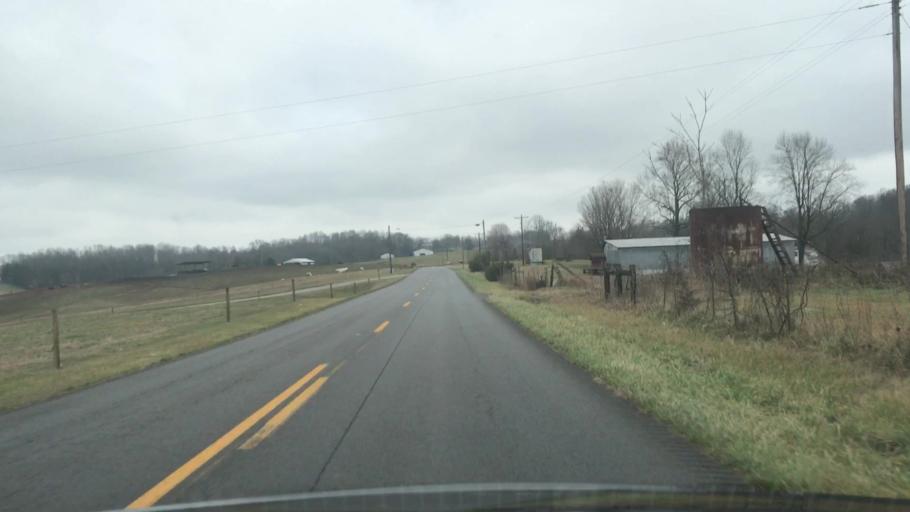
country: US
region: Kentucky
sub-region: Monroe County
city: Tompkinsville
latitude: 36.7928
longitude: -85.7378
